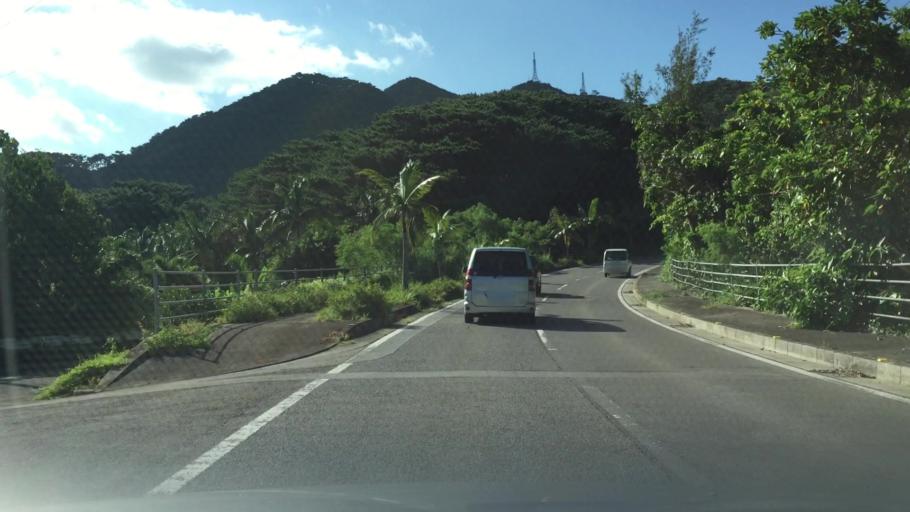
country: JP
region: Okinawa
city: Ishigaki
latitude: 24.4467
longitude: 124.1339
